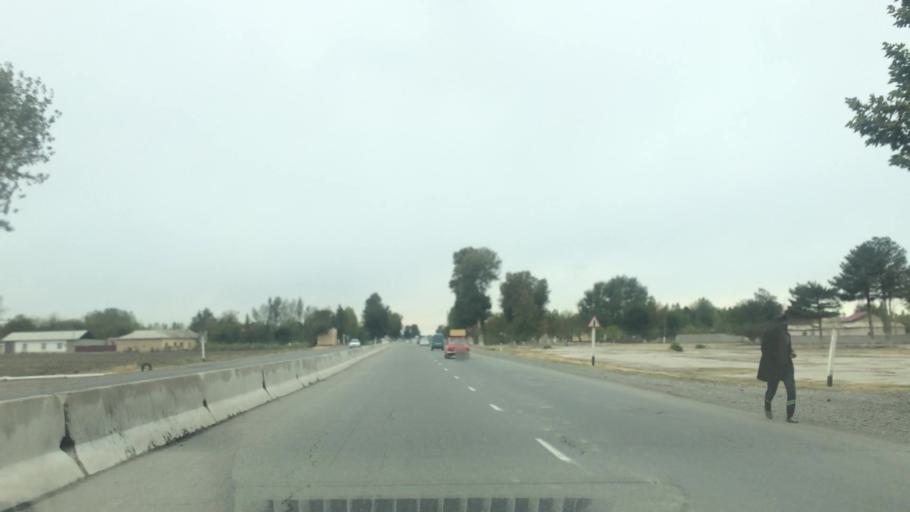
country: UZ
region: Samarqand
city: Jomboy
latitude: 39.7314
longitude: 67.1570
